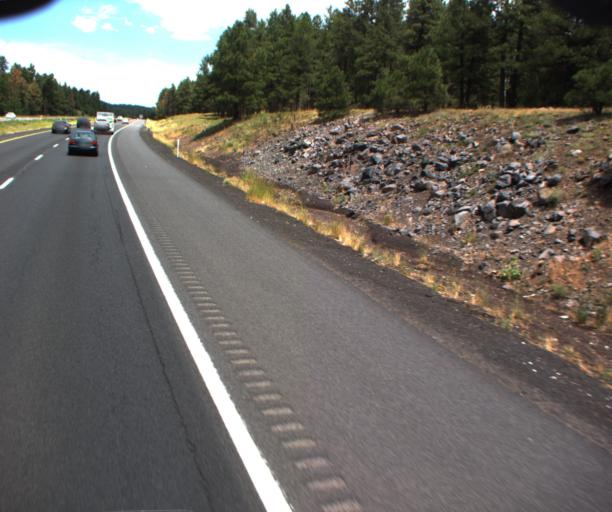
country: US
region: Arizona
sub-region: Coconino County
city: Sedona
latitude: 34.9596
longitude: -111.6790
